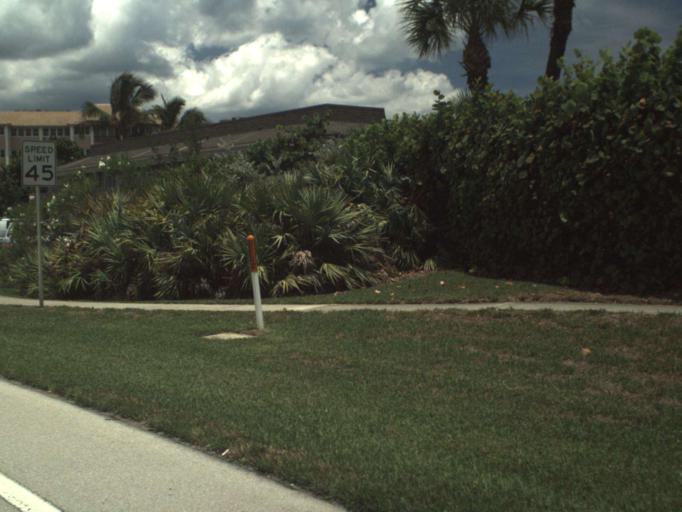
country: US
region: Florida
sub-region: Martin County
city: Sewall's Point
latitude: 27.2224
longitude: -80.1798
